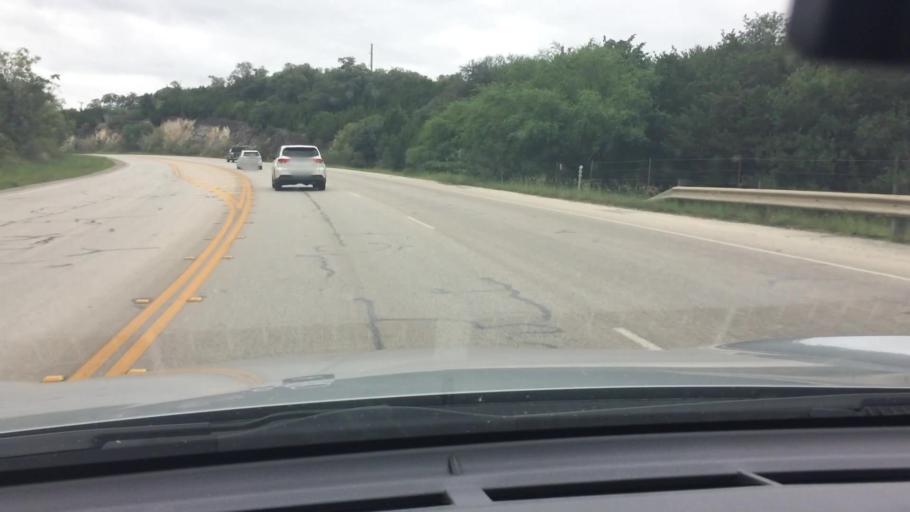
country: US
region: Texas
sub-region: Bexar County
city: Live Oak
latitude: 29.6100
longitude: -98.3679
